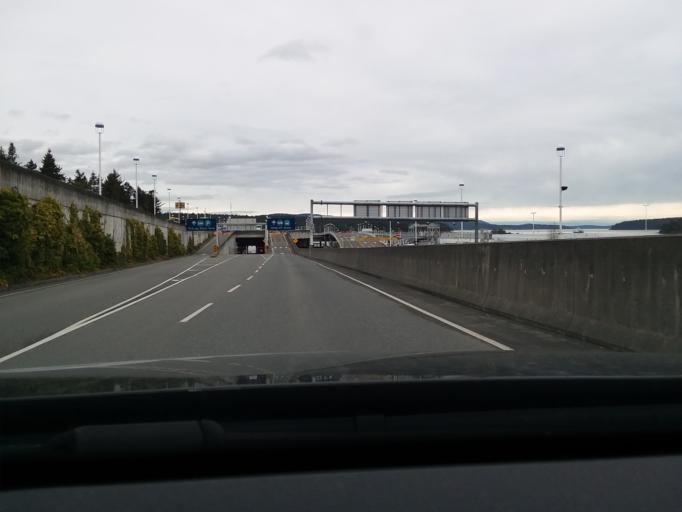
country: CA
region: British Columbia
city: North Saanich
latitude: 48.6861
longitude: -123.4107
